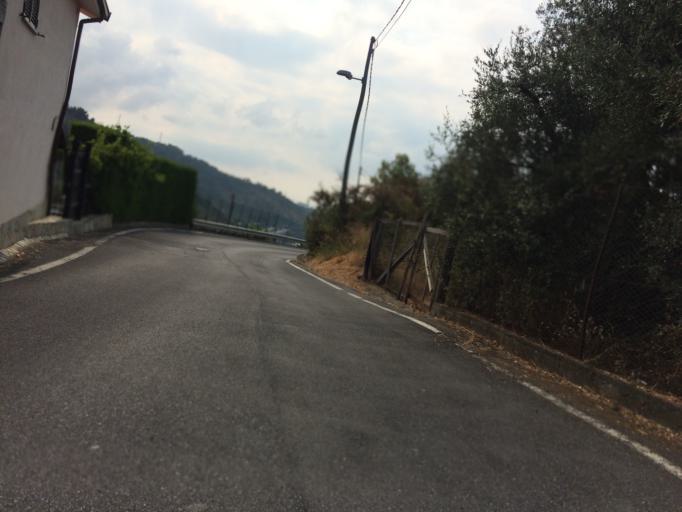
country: IT
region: Liguria
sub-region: Provincia di Imperia
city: San Remo
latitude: 43.8396
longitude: 7.7513
